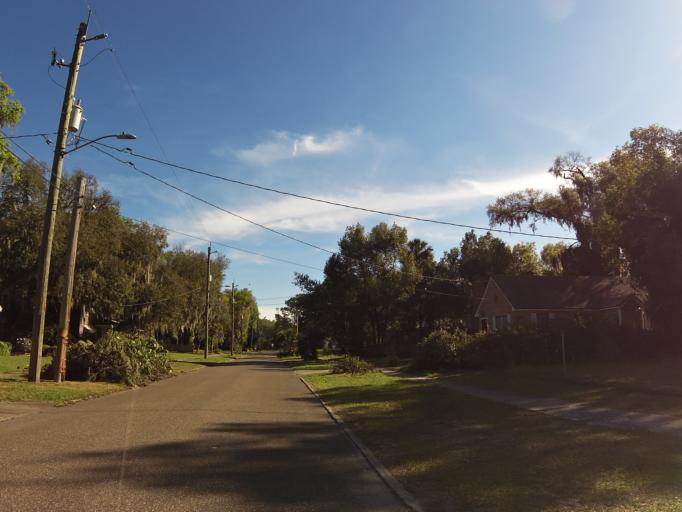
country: US
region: Florida
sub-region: Duval County
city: Jacksonville
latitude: 30.3828
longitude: -81.6472
